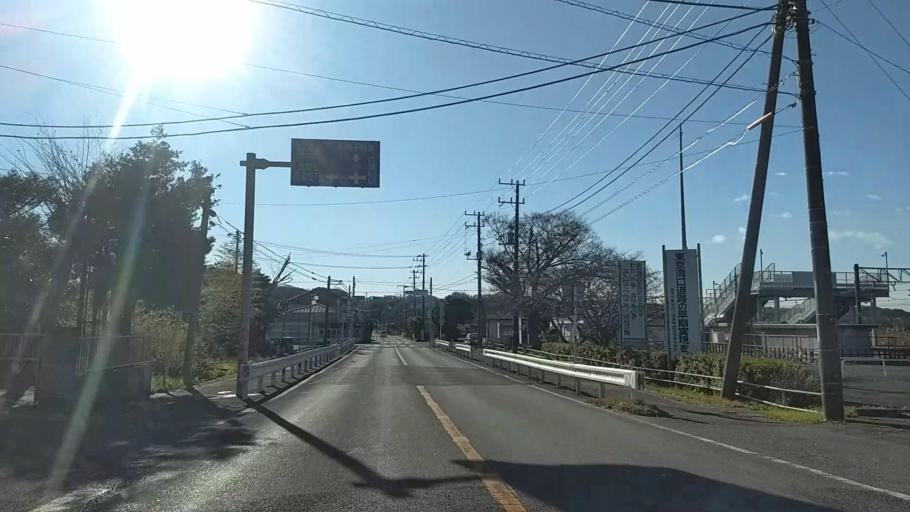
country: JP
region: Chiba
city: Kimitsu
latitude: 35.2616
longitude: 139.8761
